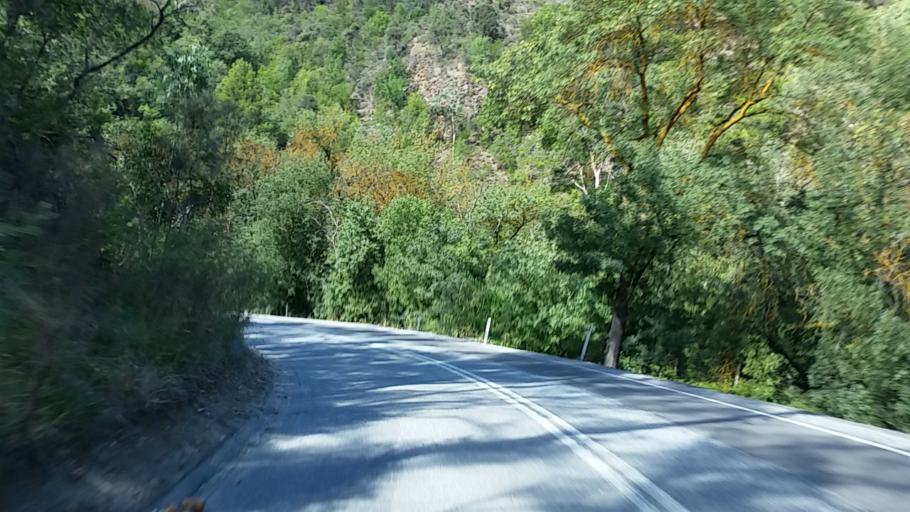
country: AU
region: South Australia
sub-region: Campbelltown
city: Athelstone
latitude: -34.8619
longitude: 138.7476
